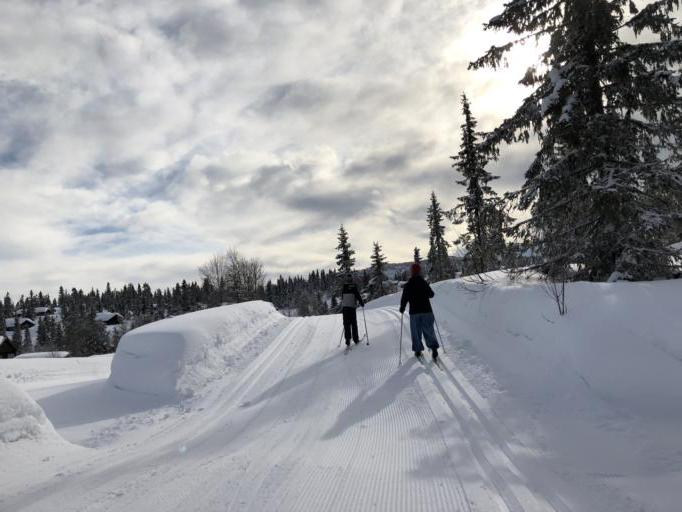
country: NO
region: Oppland
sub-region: Gausdal
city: Segalstad bru
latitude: 61.3159
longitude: 10.0645
